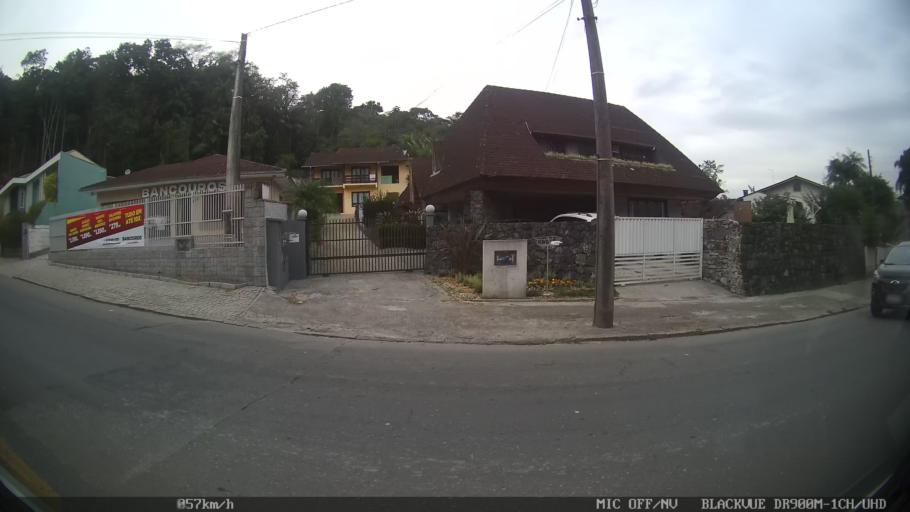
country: BR
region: Santa Catarina
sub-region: Joinville
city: Joinville
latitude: -26.2851
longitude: -48.8669
